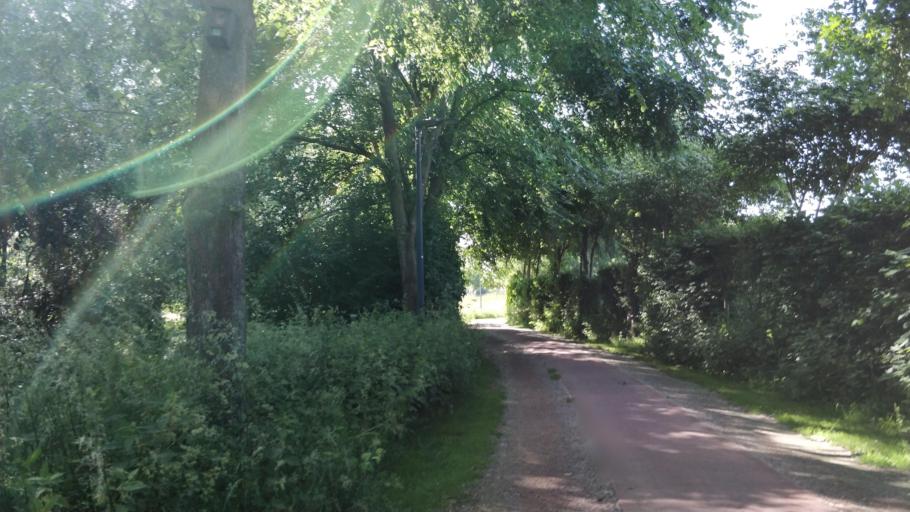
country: BE
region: Flanders
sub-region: Provincie West-Vlaanderen
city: Lendelede
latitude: 50.8443
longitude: 3.2172
